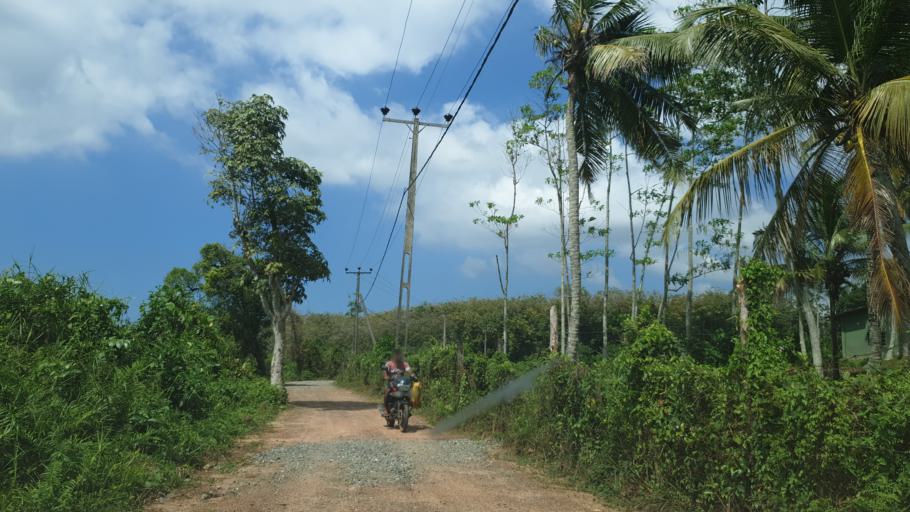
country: LK
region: Western
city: Panadura
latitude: 6.6782
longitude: 79.9615
